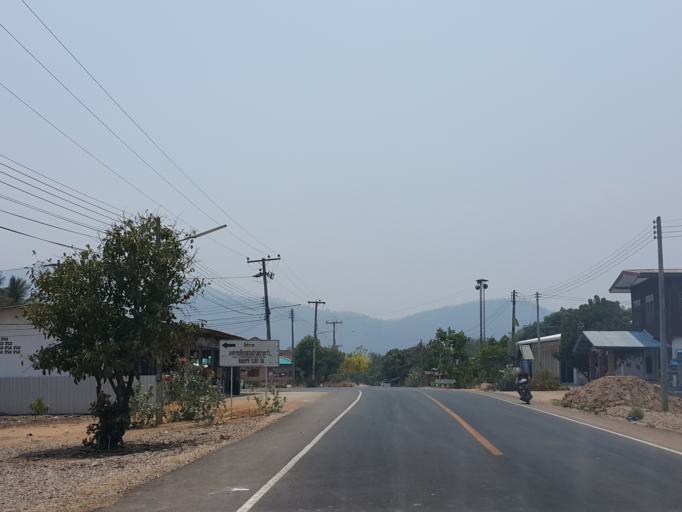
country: TH
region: Kamphaeng Phet
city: Pang Sila Thong
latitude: 16.0262
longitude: 99.3677
